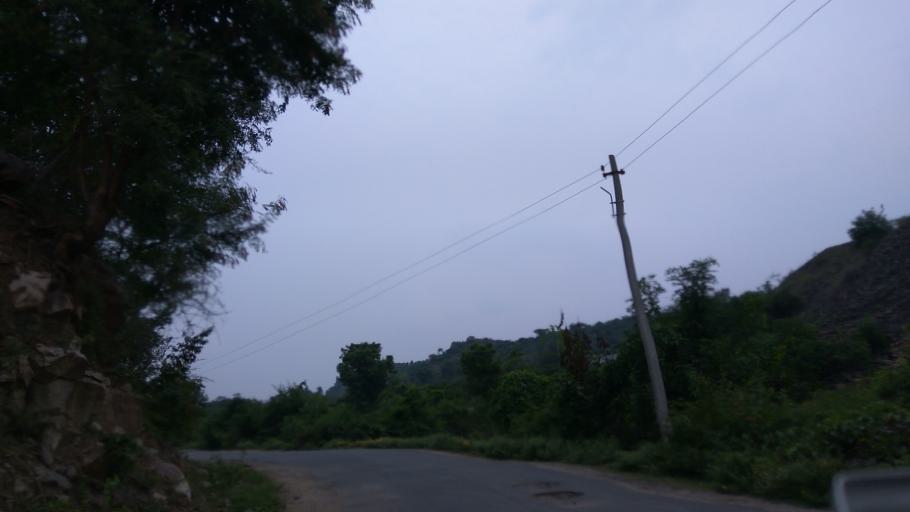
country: IN
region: Tamil Nadu
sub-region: Dharmapuri
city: Dharmapuri
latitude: 12.0157
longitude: 78.1260
